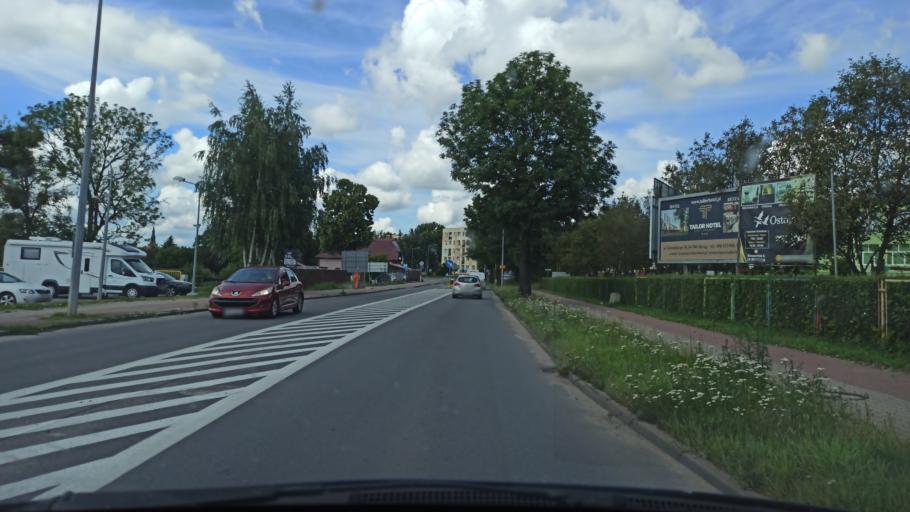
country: PL
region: Warmian-Masurian Voivodeship
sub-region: Powiat ostrodzki
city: Morag
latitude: 53.9078
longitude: 19.9363
